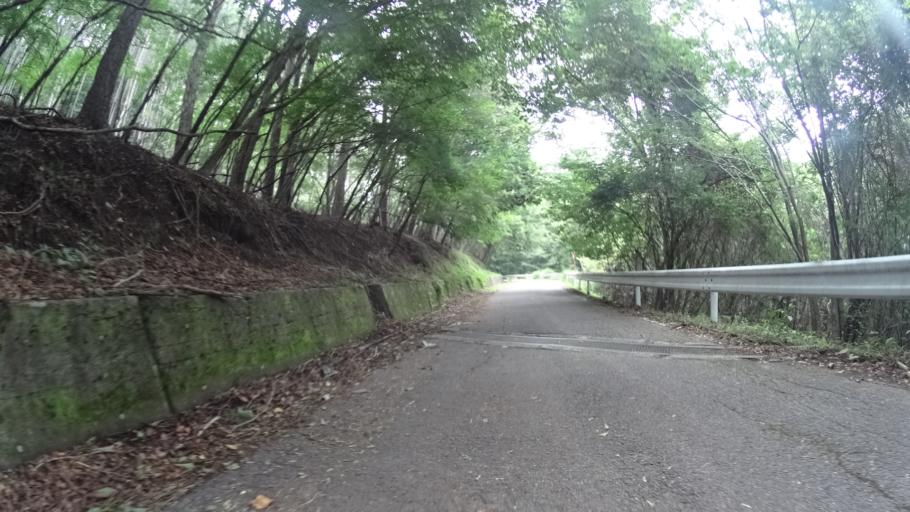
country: JP
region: Yamanashi
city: Kofu-shi
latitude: 35.8542
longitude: 138.5736
